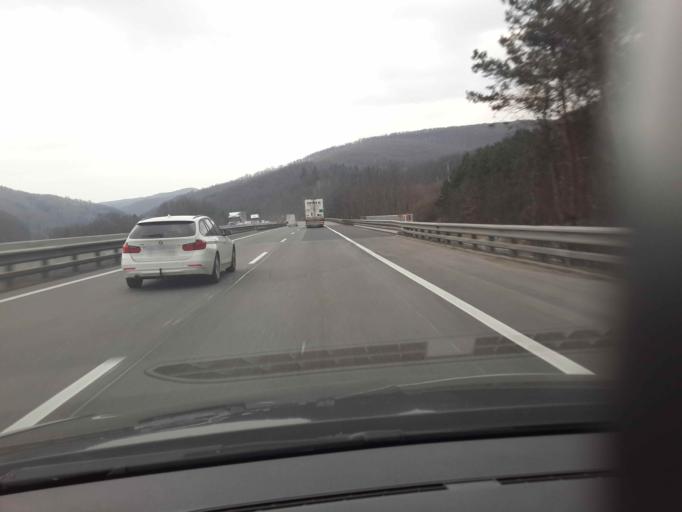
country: AT
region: Lower Austria
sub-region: Politischer Bezirk Baden
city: Alland
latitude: 48.0678
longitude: 16.0675
